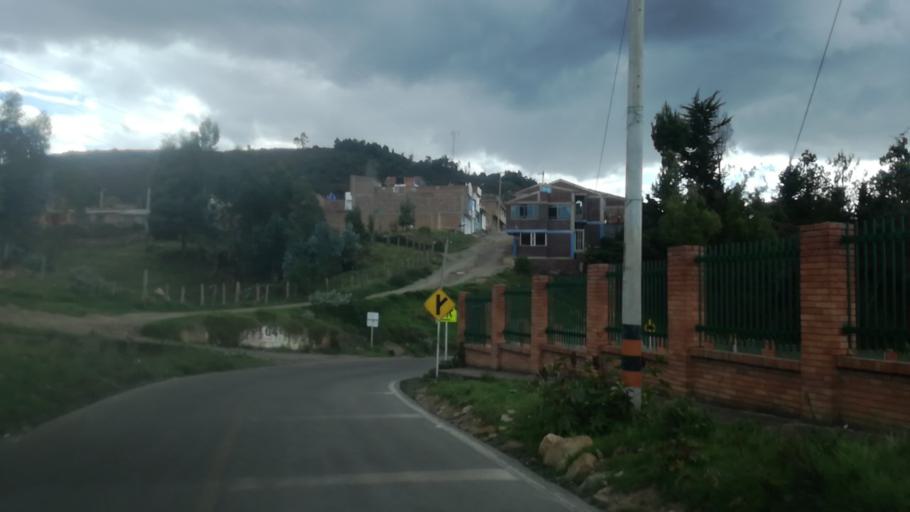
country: CO
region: Boyaca
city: Socha Viejo
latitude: 5.9963
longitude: -72.6888
